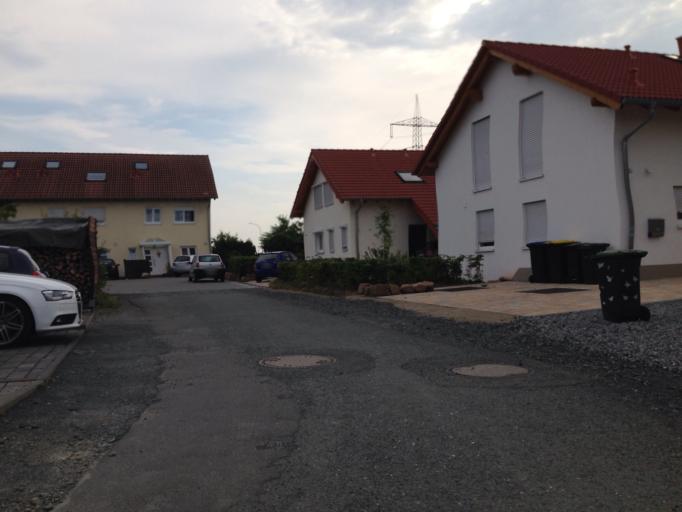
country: DE
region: Hesse
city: Allendorf an der Lahn
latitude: 50.5557
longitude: 8.6336
